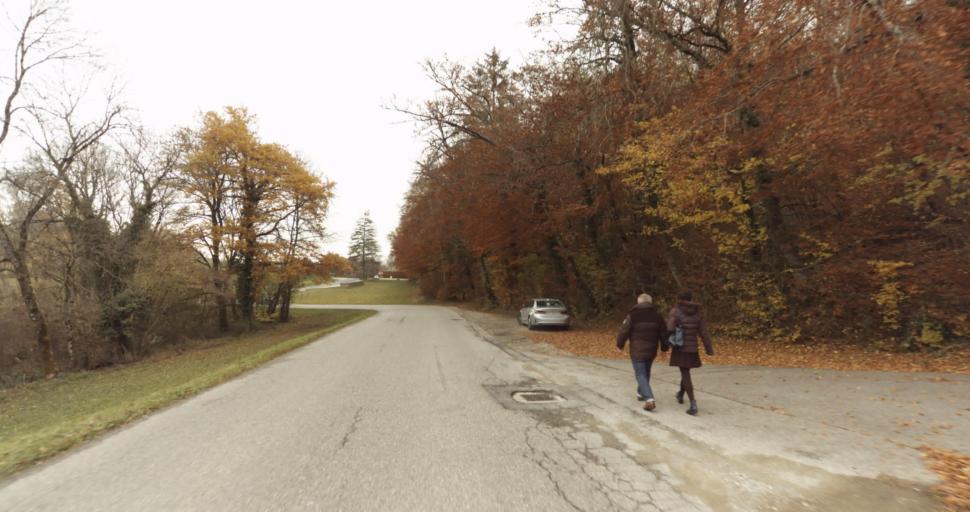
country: FR
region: Rhone-Alpes
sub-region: Departement de la Haute-Savoie
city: Saint-Martin-Bellevue
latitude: 45.9639
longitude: 6.1451
